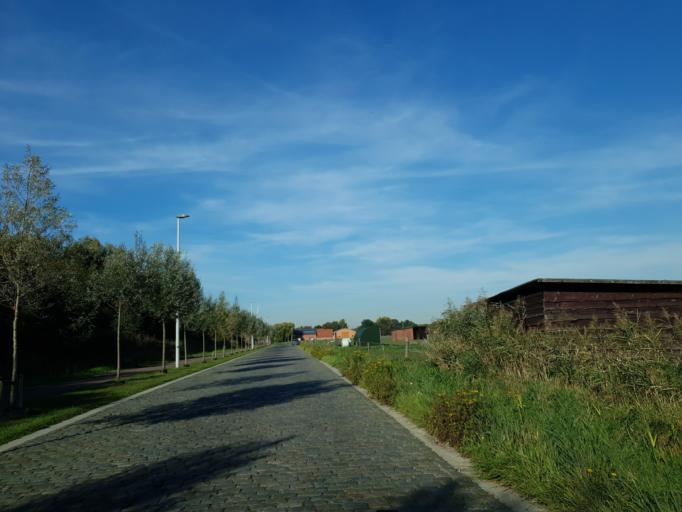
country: BE
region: Flanders
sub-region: Provincie Antwerpen
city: Stabroek
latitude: 51.3470
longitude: 4.3061
